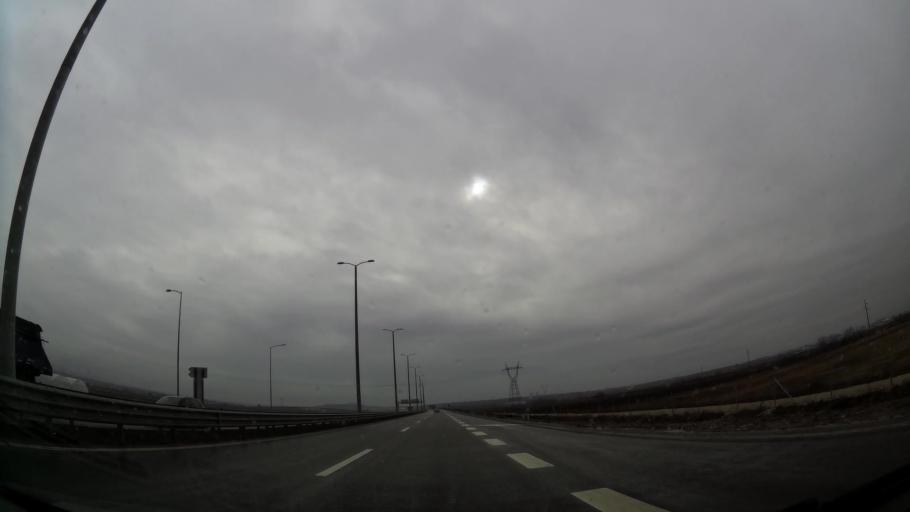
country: XK
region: Pristina
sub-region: Lipjan
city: Lipljan
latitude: 42.4611
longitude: 21.1794
